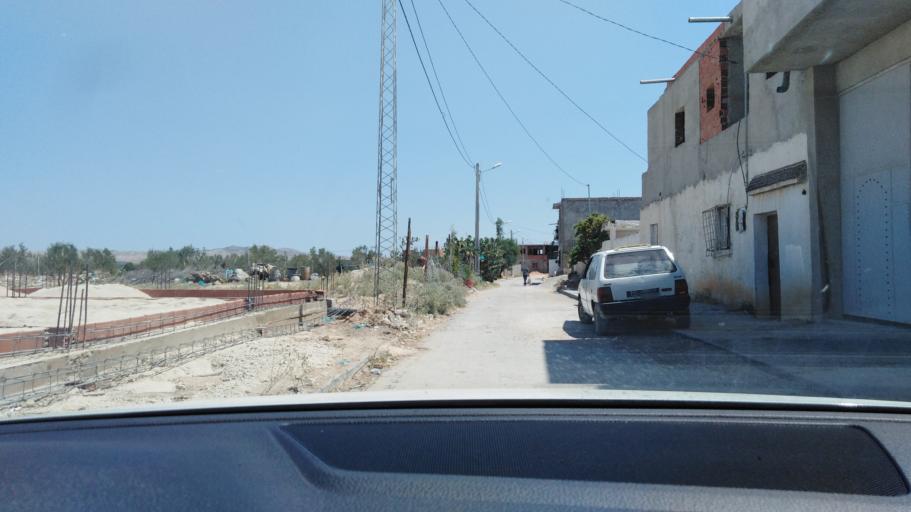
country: TN
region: Al Qayrawan
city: Sbikha
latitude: 36.1170
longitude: 10.0988
